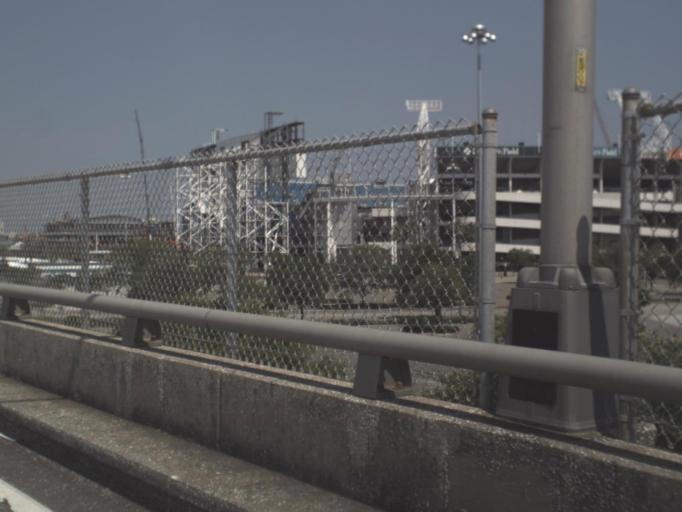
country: US
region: Florida
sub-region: Duval County
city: Jacksonville
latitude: 30.3208
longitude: -81.6345
